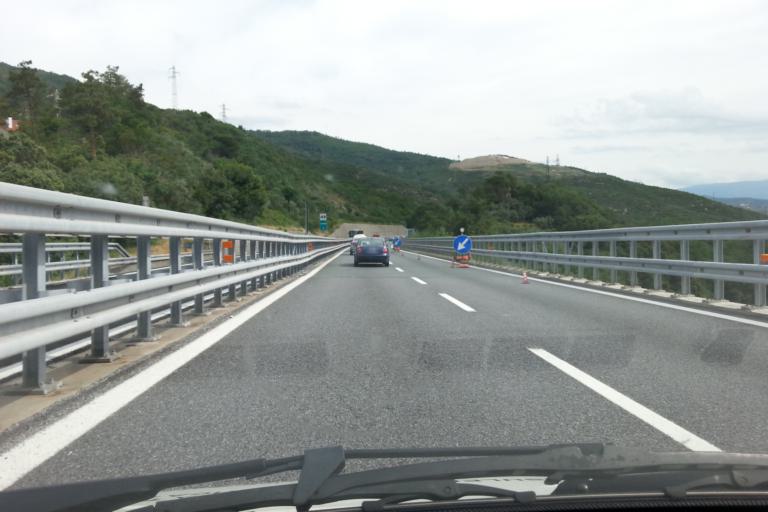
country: IT
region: Liguria
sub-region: Provincia di Savona
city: Valle di Vado
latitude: 44.2577
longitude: 8.4069
